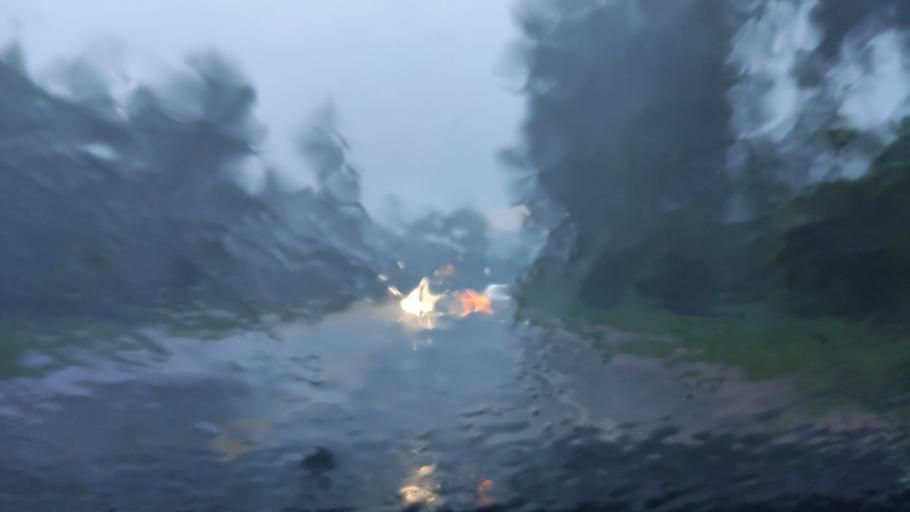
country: BR
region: Sao Paulo
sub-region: Braganca Paulista
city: Braganca Paulista
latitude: -22.7735
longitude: -46.5620
